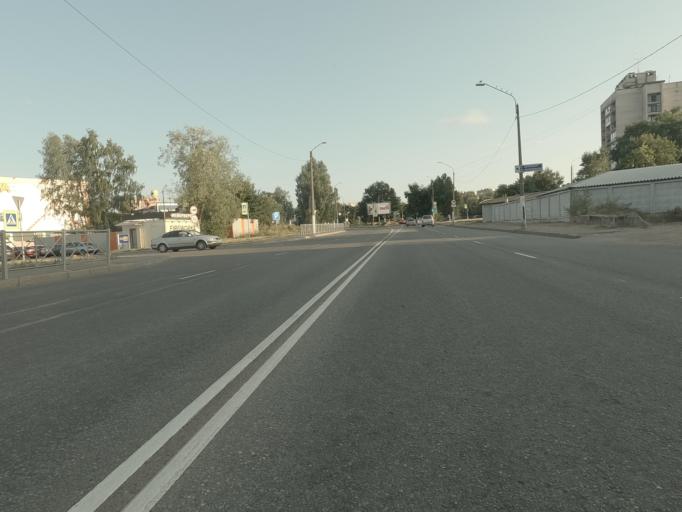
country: RU
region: Leningrad
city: Vyborg
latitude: 60.7082
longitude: 28.7709
